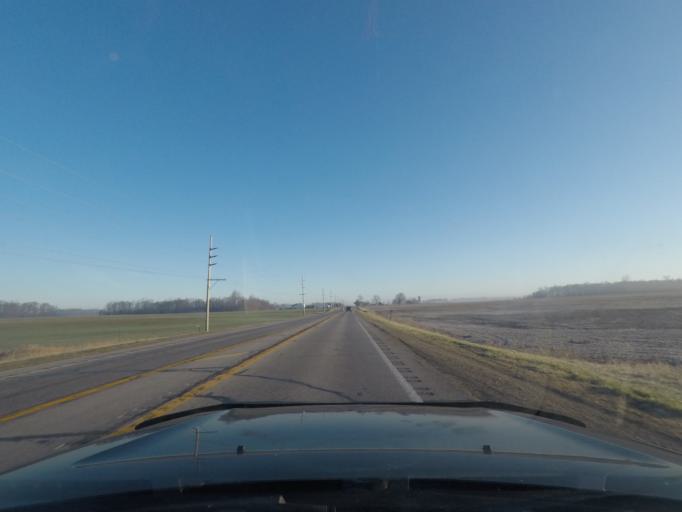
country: US
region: Indiana
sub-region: Elkhart County
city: Wakarusa
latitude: 41.4957
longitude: -86.0019
